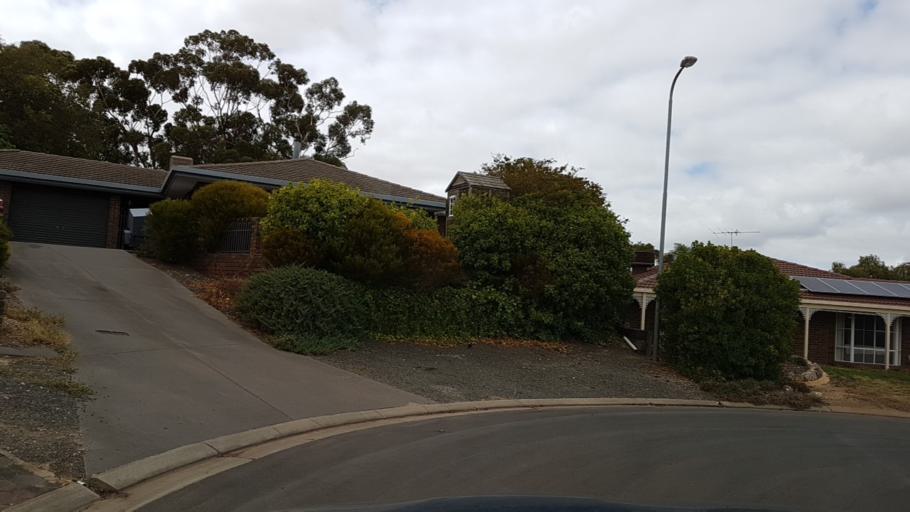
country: AU
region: South Australia
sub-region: Gawler
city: Gawler
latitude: -34.6081
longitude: 138.7592
